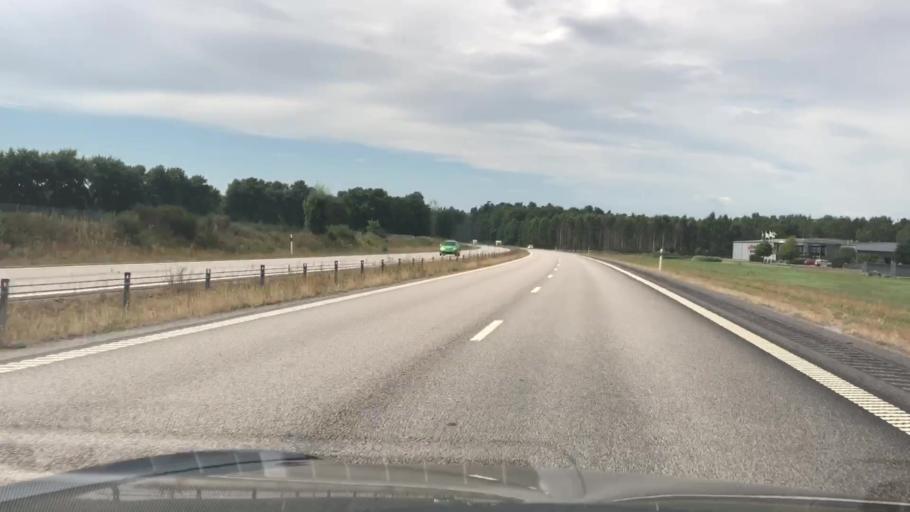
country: SE
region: Skane
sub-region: Bromolla Kommun
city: Bromoella
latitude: 56.0628
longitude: 14.4682
